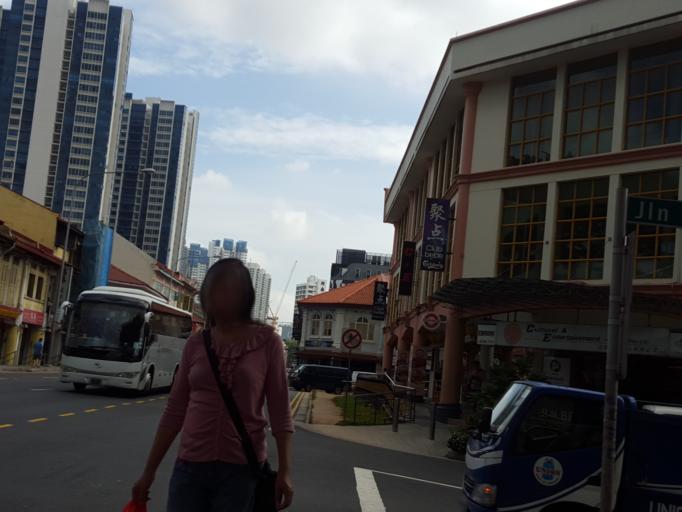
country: SG
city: Singapore
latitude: 1.3077
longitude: 103.8569
